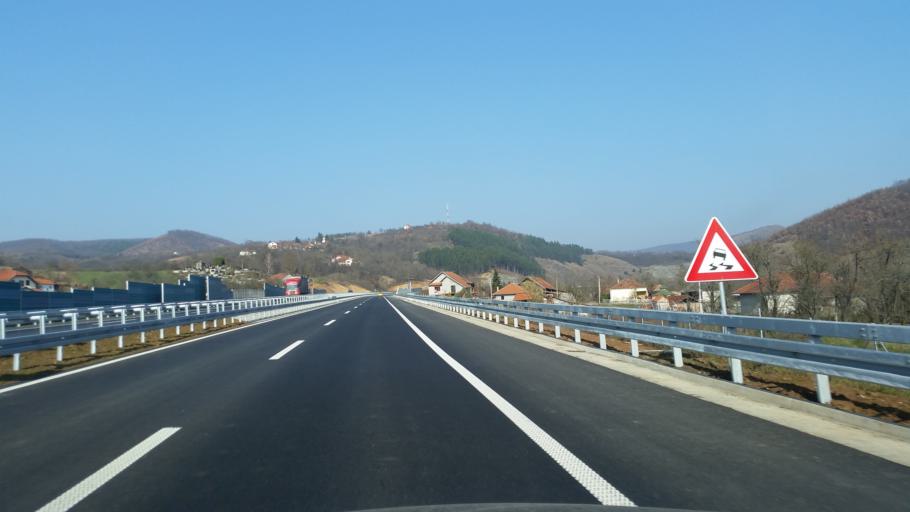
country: RS
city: Prislonica
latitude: 43.9661
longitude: 20.3961
